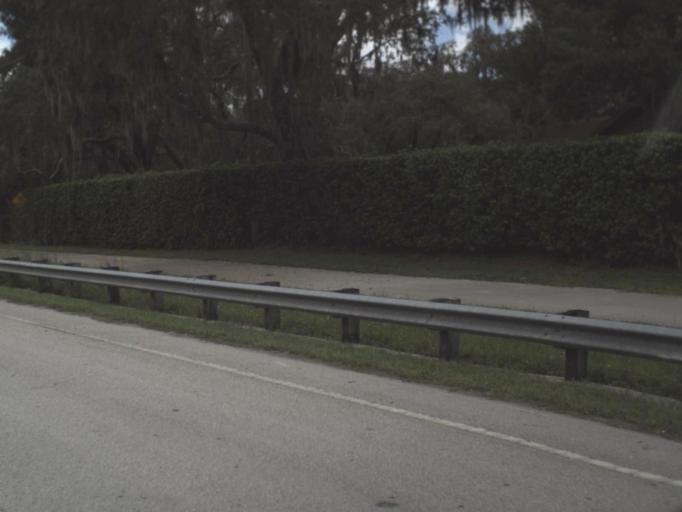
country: US
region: Florida
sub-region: Pinellas County
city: East Lake
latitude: 28.1220
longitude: -82.6960
